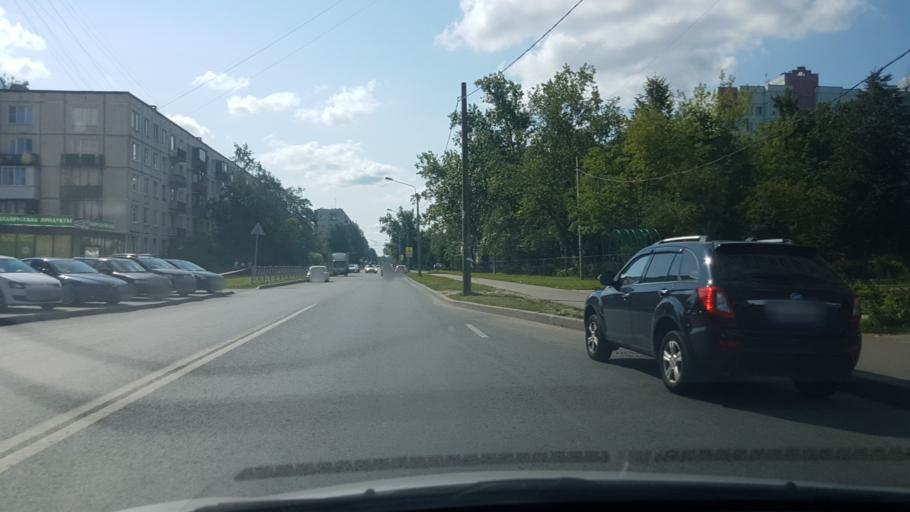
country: RU
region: St.-Petersburg
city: Sosnovaya Polyana
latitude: 59.8340
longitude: 30.1566
